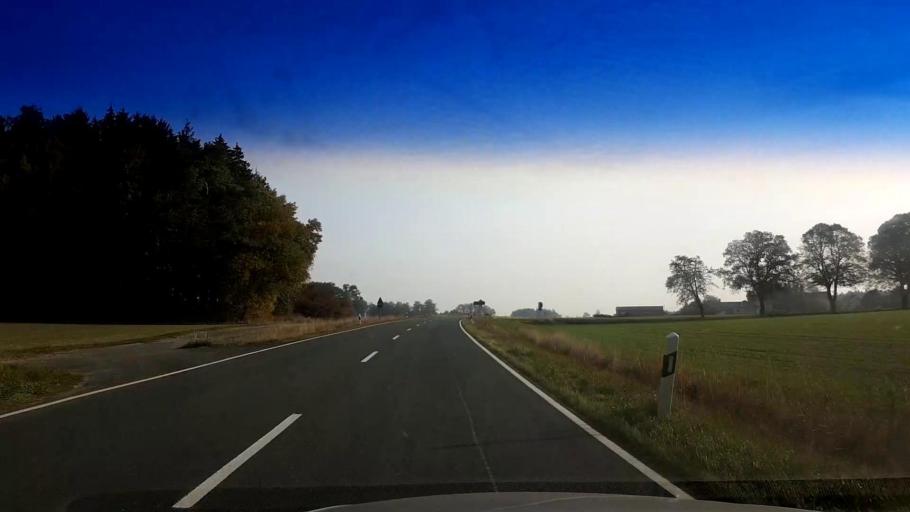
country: DE
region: Bavaria
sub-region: Upper Franconia
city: Stadelhofen
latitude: 50.0057
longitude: 11.1689
